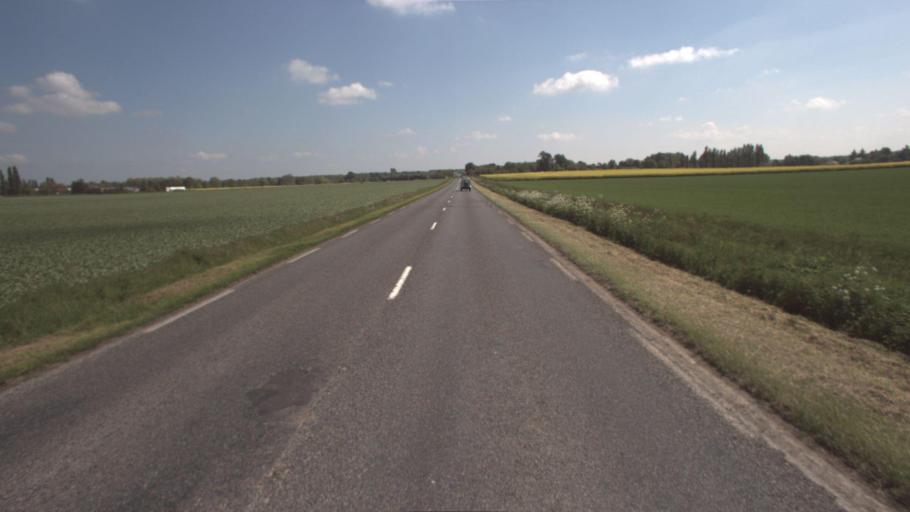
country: FR
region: Ile-de-France
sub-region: Departement de Seine-et-Marne
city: Guignes
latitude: 48.6316
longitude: 2.7811
